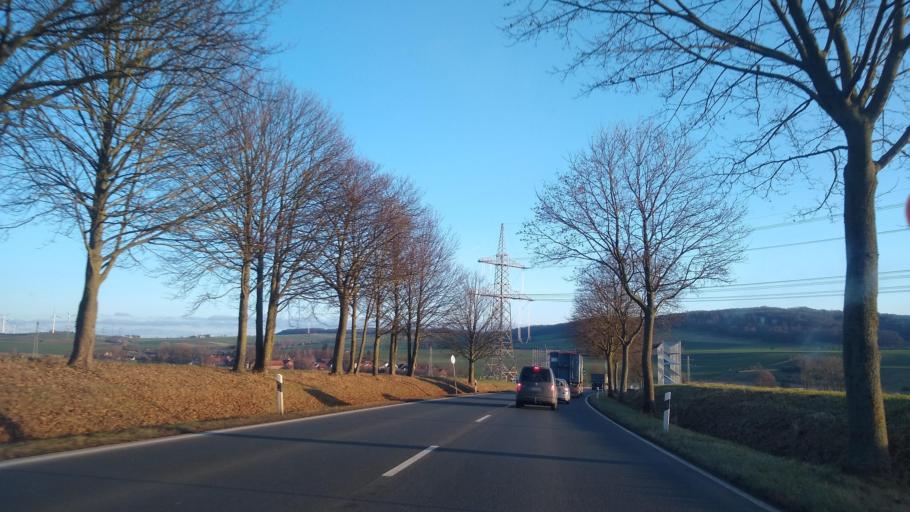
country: DE
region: Lower Saxony
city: Einbeck
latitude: 51.8671
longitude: 9.8434
